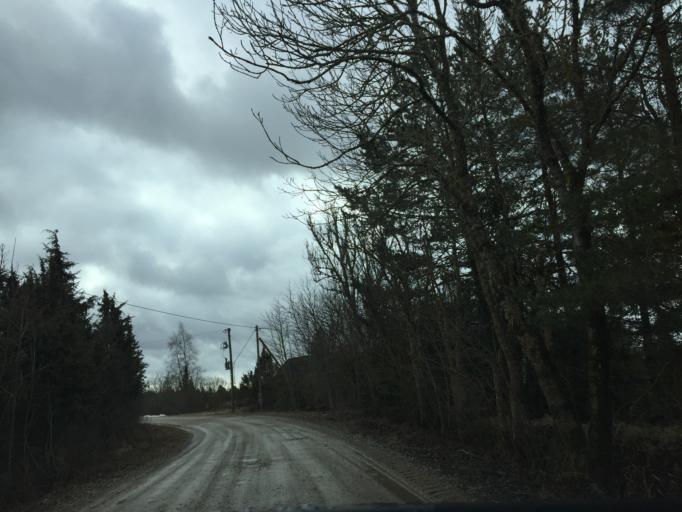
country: EE
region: Laeaene
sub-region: Haapsalu linn
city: Haapsalu
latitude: 58.6827
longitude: 23.5287
